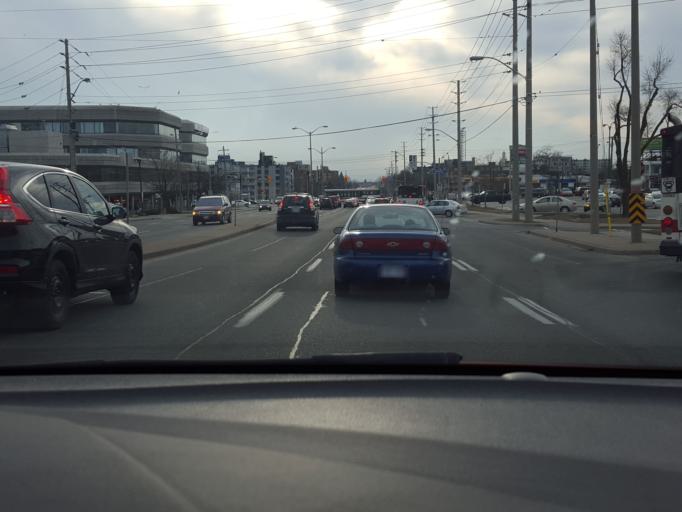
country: CA
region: Ontario
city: Scarborough
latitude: 43.7329
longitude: -79.2657
